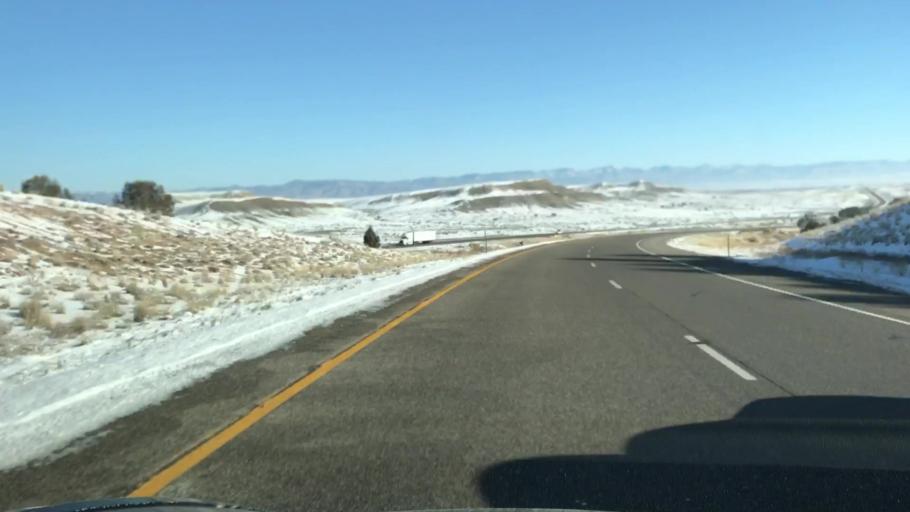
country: US
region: Colorado
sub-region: Mesa County
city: Loma
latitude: 39.2202
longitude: -108.9584
